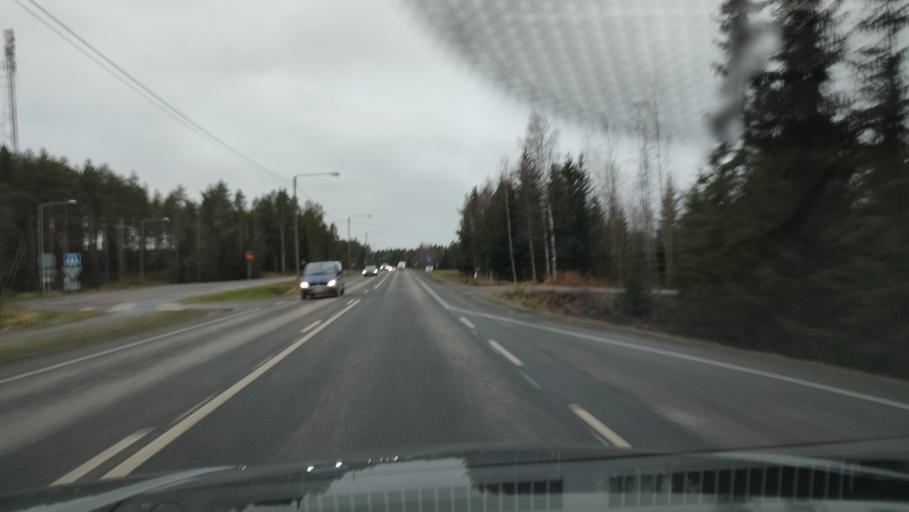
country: FI
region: Southern Ostrobothnia
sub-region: Seinaejoki
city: Seinaejoki
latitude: 62.7787
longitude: 22.6967
